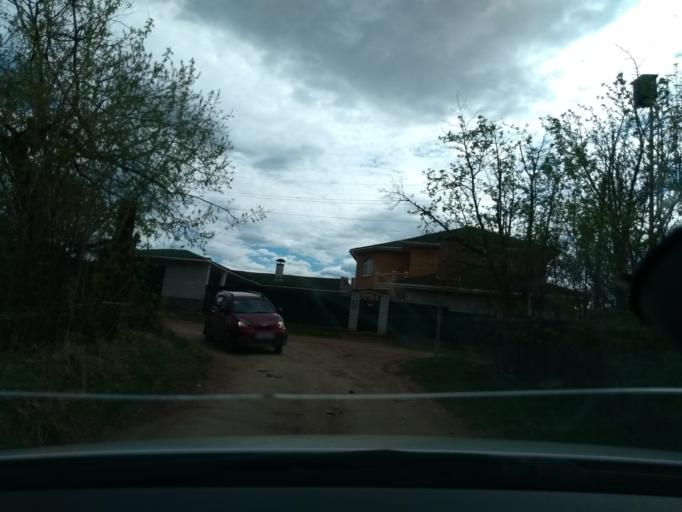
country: RU
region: Perm
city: Lobanovo
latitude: 57.8669
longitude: 56.3052
